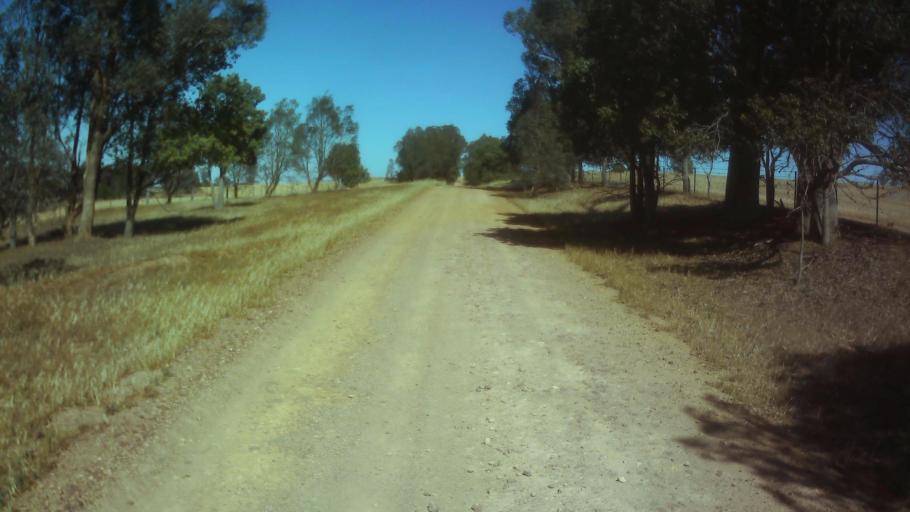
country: AU
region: New South Wales
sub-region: Weddin
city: Grenfell
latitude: -33.9935
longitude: 148.3527
